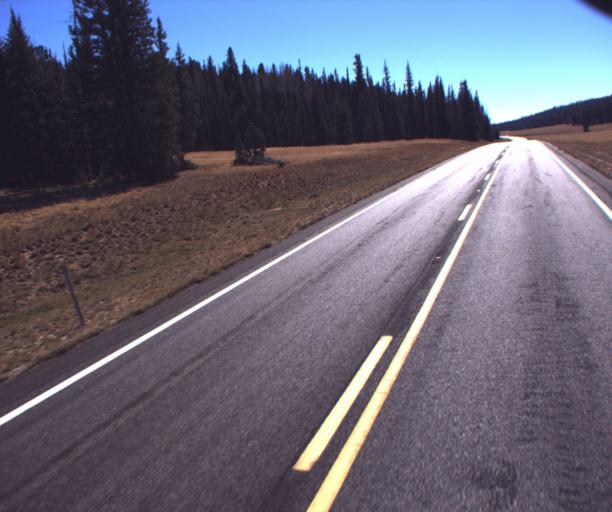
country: US
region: Arizona
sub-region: Coconino County
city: Grand Canyon
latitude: 36.3818
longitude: -112.1261
